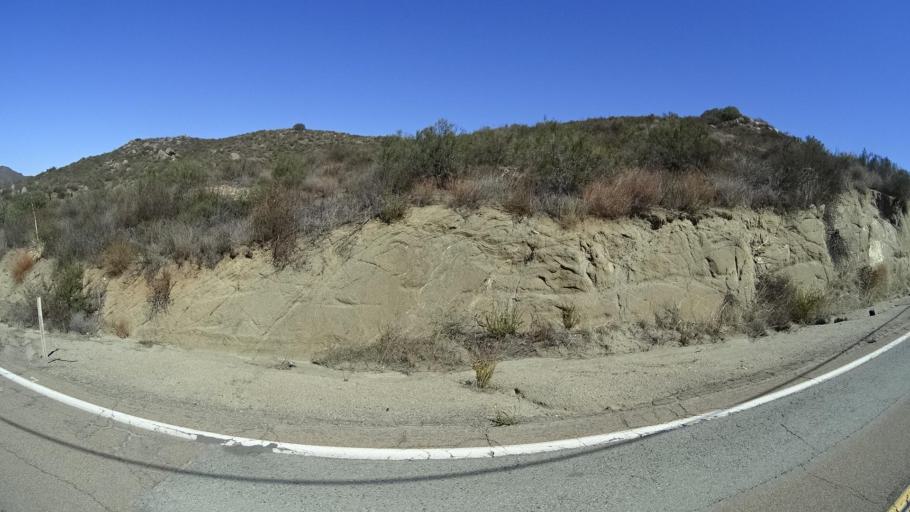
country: US
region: California
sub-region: San Diego County
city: Alpine
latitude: 32.7871
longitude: -116.7251
